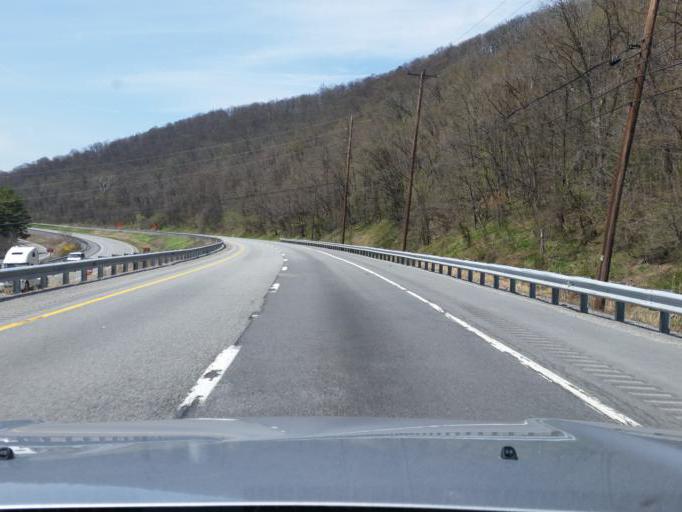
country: US
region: Pennsylvania
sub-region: Perry County
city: Newport
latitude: 40.5654
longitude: -77.1711
